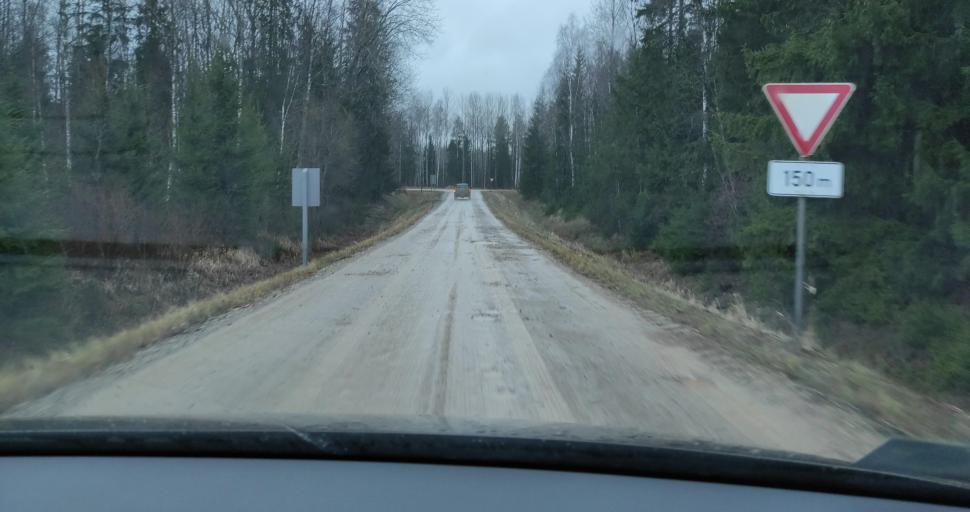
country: LV
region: Skrunda
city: Skrunda
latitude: 56.5788
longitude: 22.1391
